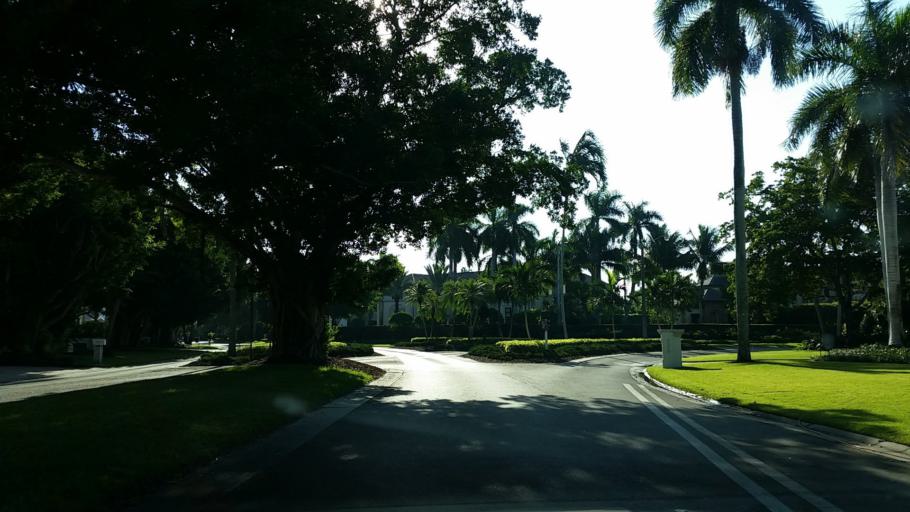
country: US
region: Florida
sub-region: Collier County
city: Naples
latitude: 26.1125
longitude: -81.7958
